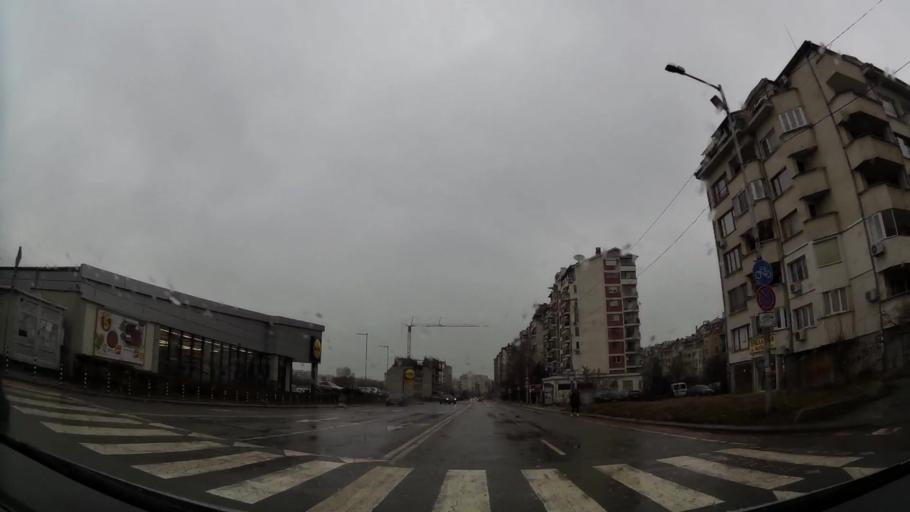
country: BG
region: Sofia-Capital
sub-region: Stolichna Obshtina
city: Sofia
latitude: 42.6355
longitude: 23.3750
